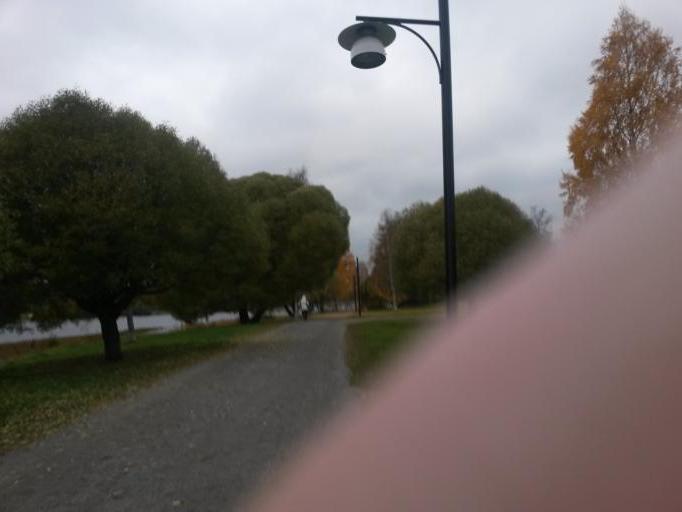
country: SE
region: Vaesterbotten
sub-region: Skelleftea Kommun
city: Skelleftea
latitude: 64.7475
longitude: 20.9665
